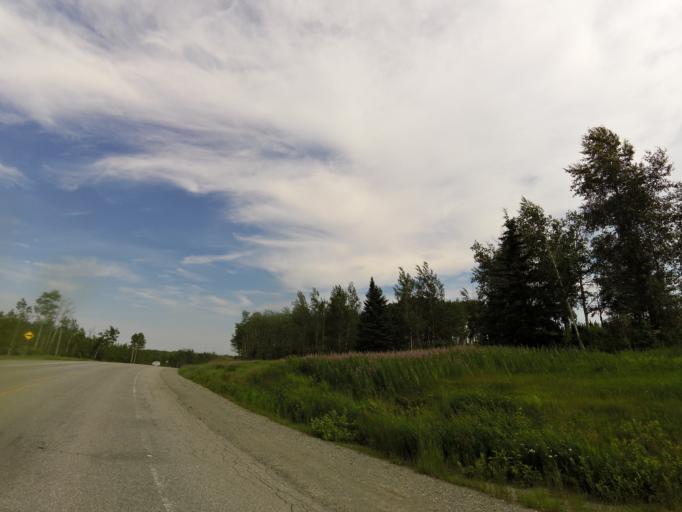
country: CA
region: Quebec
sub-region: Abitibi-Temiscamingue
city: Malartic
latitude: 48.2335
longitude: -78.4134
